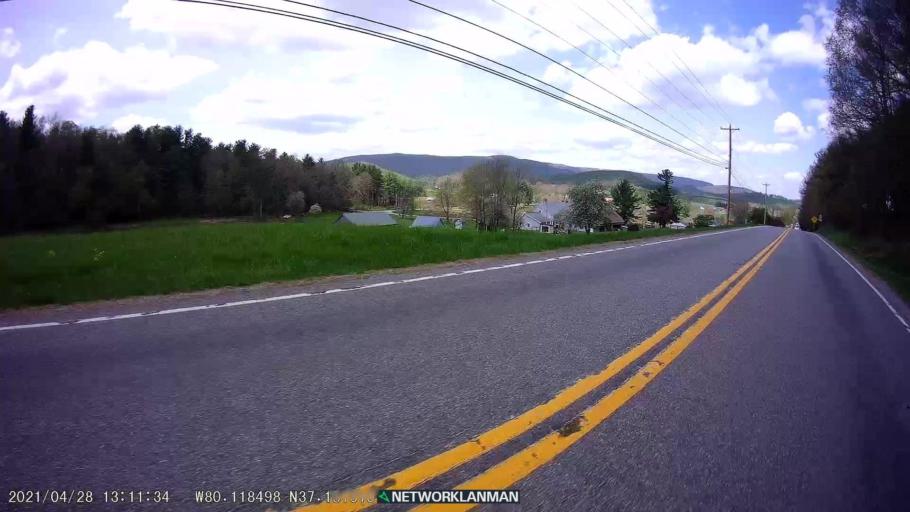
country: US
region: Virginia
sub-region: Roanoke County
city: Cave Spring
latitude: 37.1517
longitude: -80.1186
